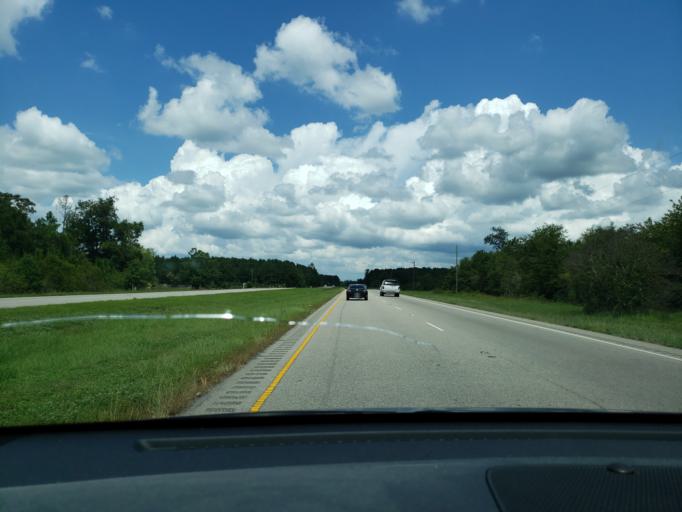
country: US
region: North Carolina
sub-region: Bladen County
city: Elizabethtown
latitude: 34.6866
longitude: -78.7412
